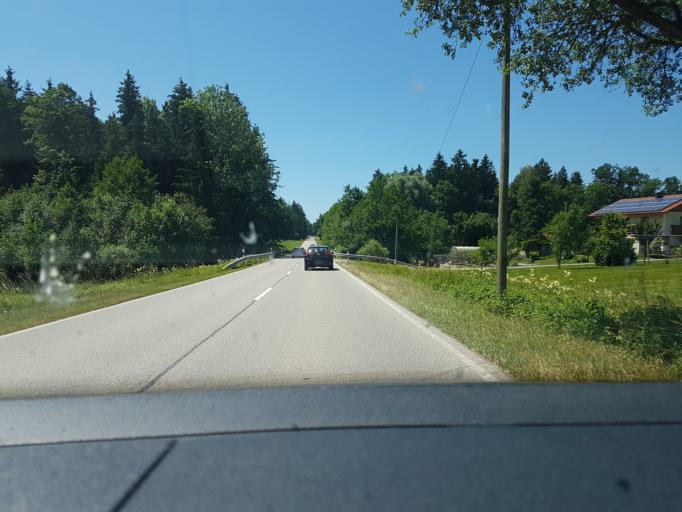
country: DE
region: Bavaria
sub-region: Upper Bavaria
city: Anger
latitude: 47.8438
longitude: 12.8716
